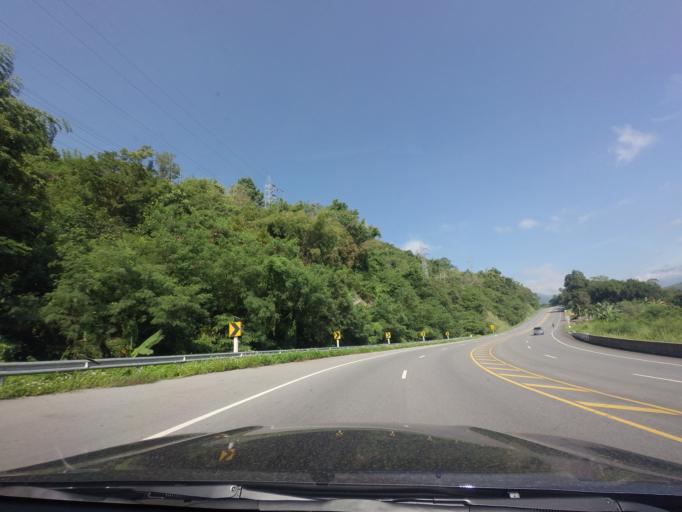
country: TH
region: Phetchabun
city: Khao Kho
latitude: 16.7792
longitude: 101.0929
